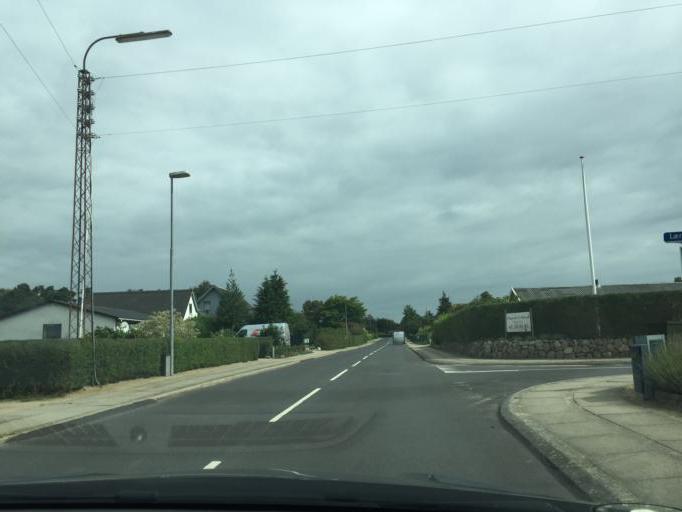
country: DK
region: South Denmark
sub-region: Assens Kommune
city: Arup
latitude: 55.3760
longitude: 10.0389
